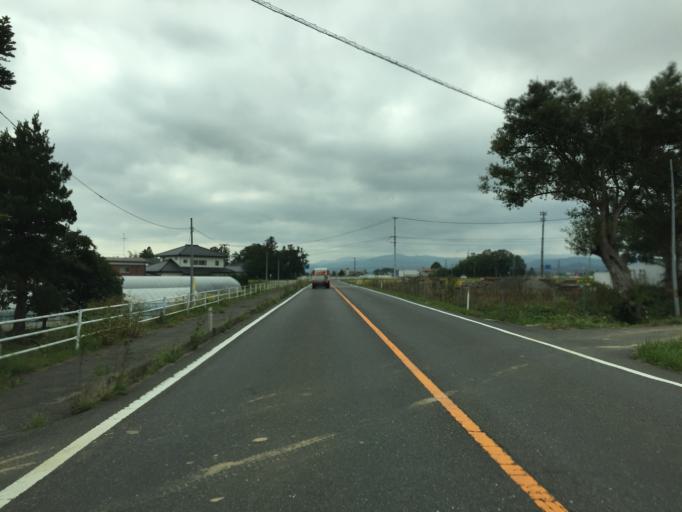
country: JP
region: Fukushima
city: Koriyama
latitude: 37.4619
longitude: 140.3523
